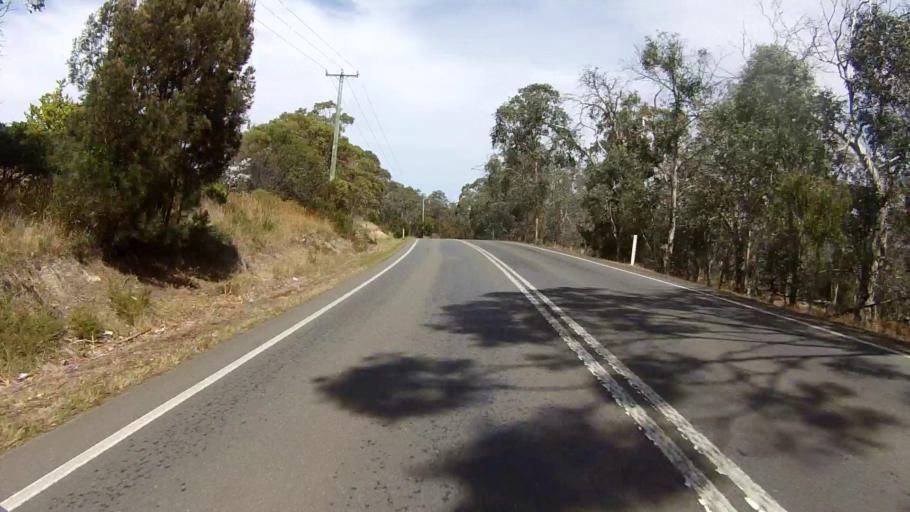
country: AU
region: Tasmania
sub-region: Clarence
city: Sandford
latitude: -42.9783
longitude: 147.5021
